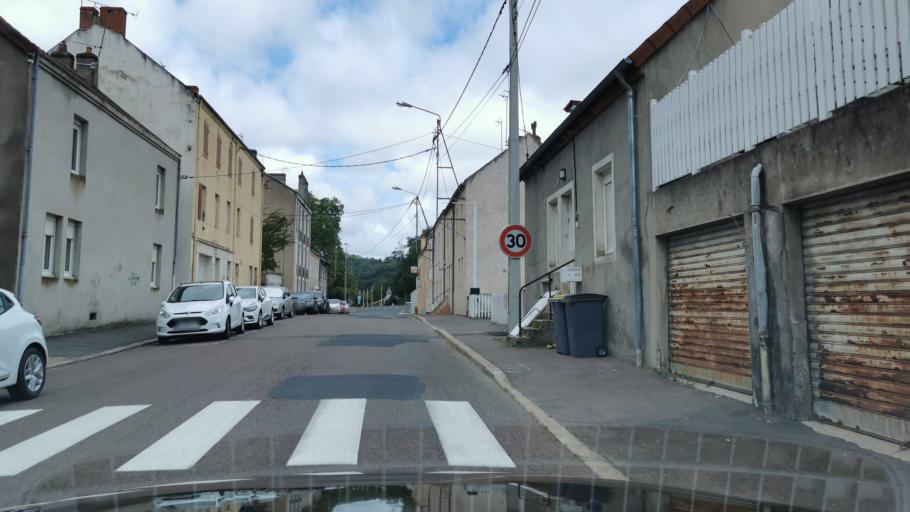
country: FR
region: Bourgogne
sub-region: Departement de Saone-et-Loire
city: Le Creusot
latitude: 46.8069
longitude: 4.4357
